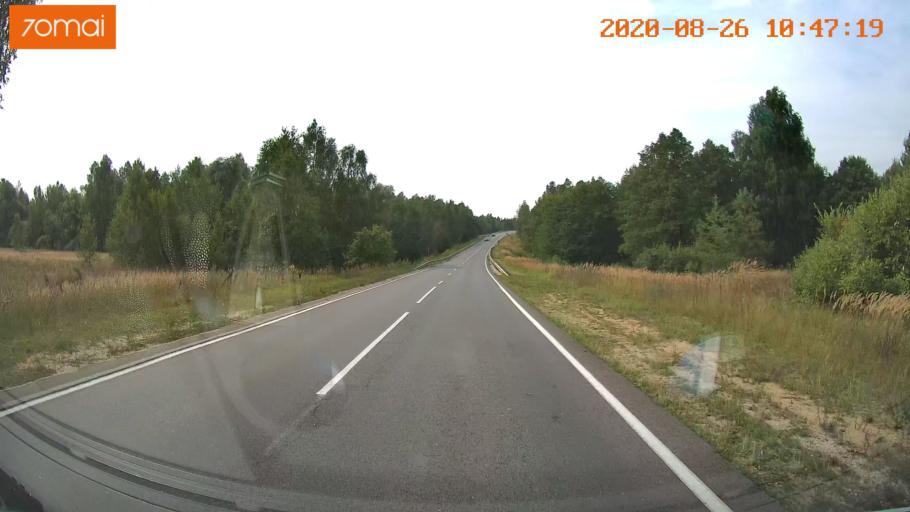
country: RU
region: Rjazan
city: Lashma
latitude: 54.7287
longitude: 41.1908
